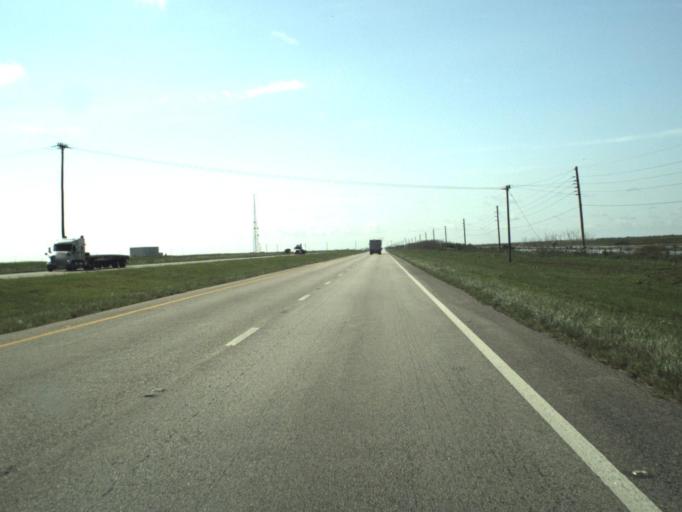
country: US
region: Florida
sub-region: Palm Beach County
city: Belle Glade Camp
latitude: 26.4438
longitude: -80.6223
